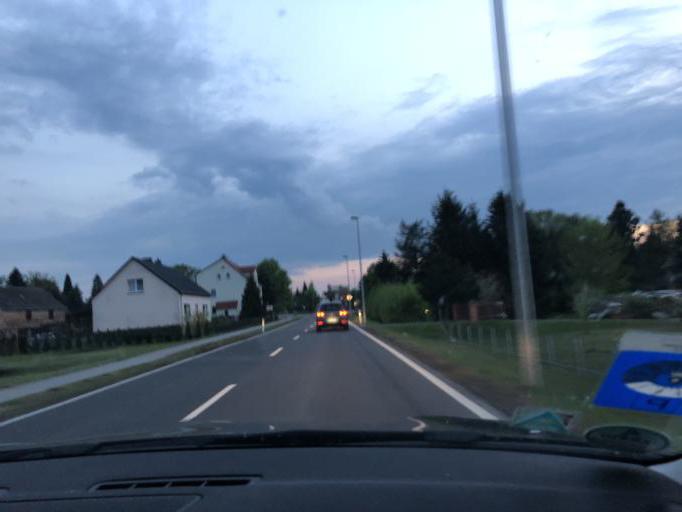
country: DE
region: Saxony
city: Krauschwitz
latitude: 51.5193
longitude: 14.7212
